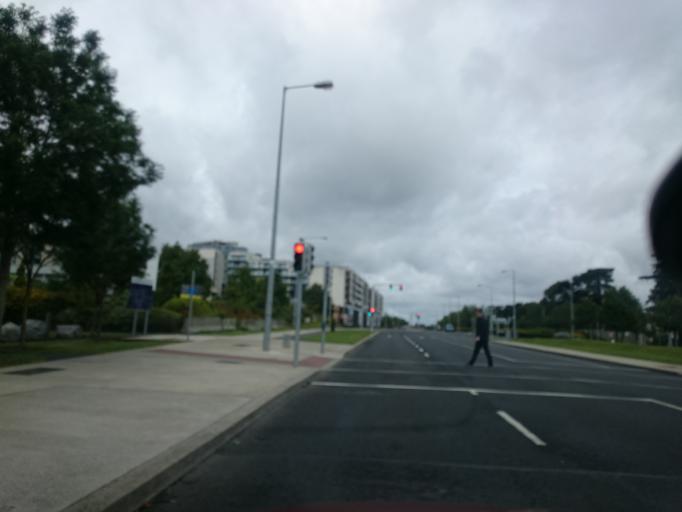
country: IE
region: Leinster
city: Sandyford
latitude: 53.2789
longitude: -6.2100
